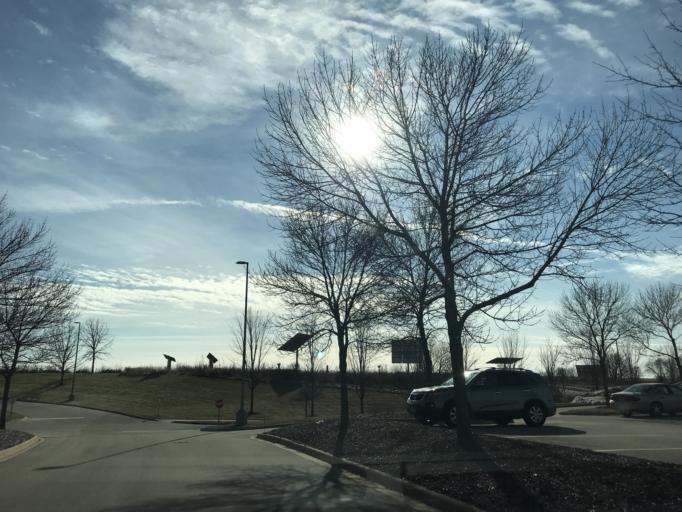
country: US
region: Wisconsin
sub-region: Dane County
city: Windsor
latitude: 43.1507
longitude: -89.2977
